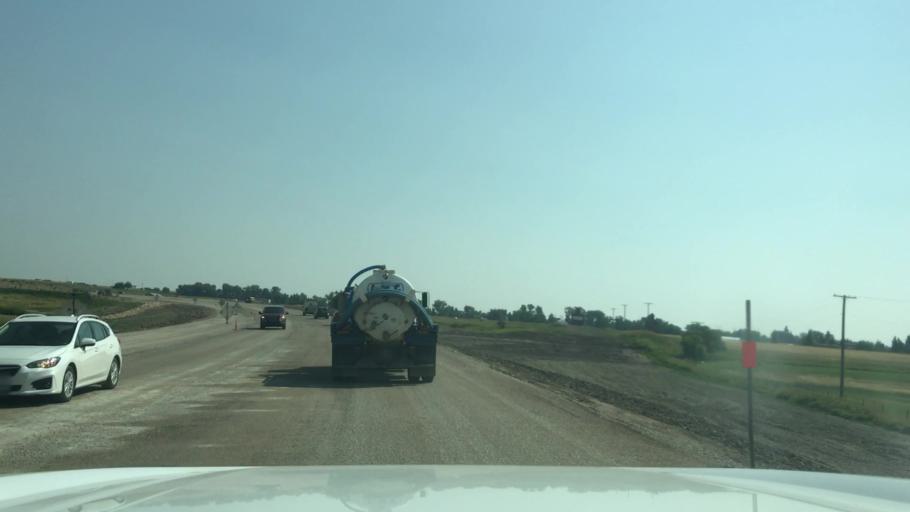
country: US
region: Montana
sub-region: Judith Basin County
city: Stanford
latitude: 47.0091
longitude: -109.8721
